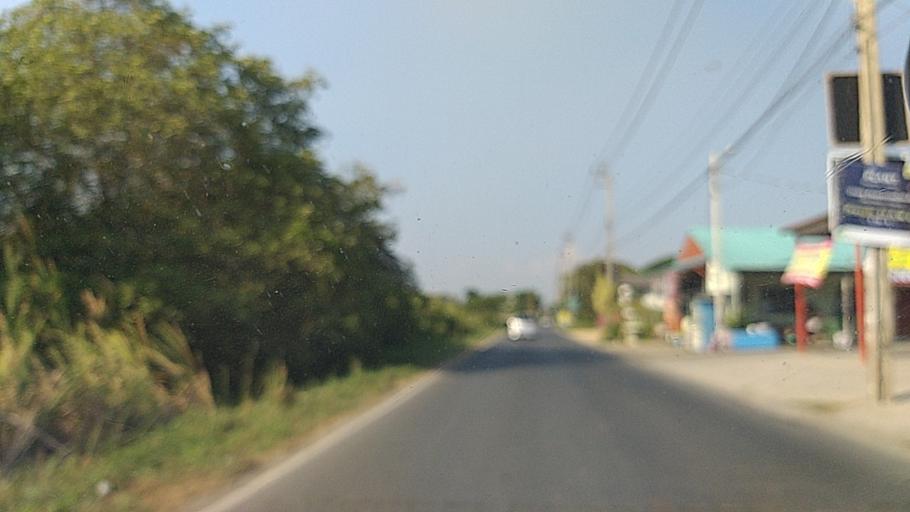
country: TH
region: Nonthaburi
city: Bang Bua Thong
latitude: 13.9390
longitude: 100.3828
